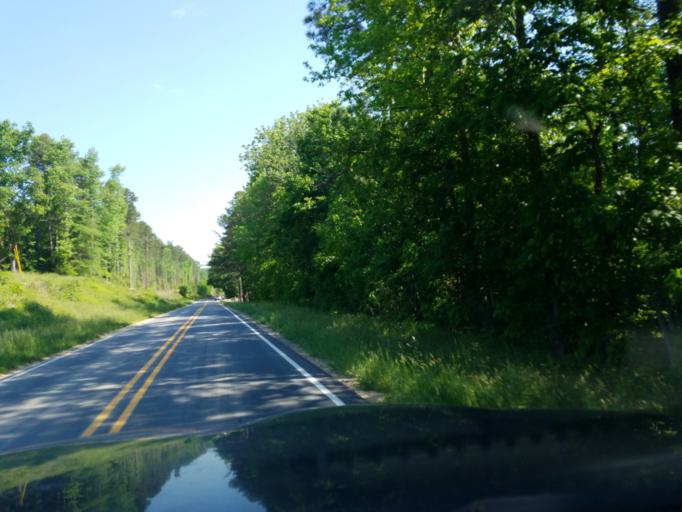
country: US
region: North Carolina
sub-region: Vance County
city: Henderson
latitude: 36.3772
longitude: -78.4462
